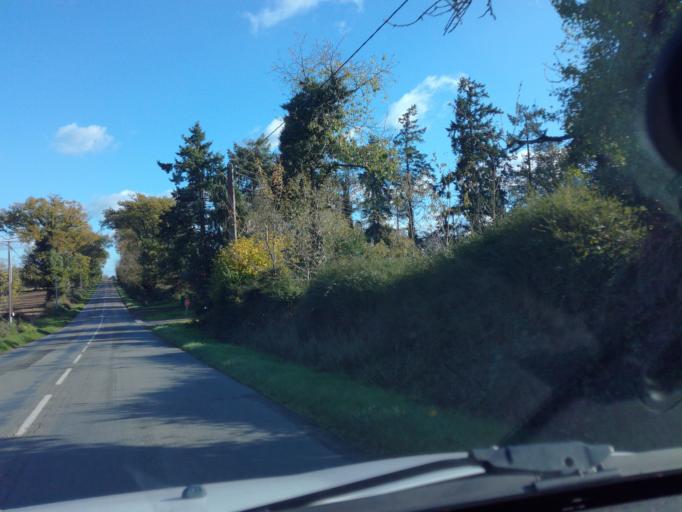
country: FR
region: Brittany
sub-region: Departement d'Ille-et-Vilaine
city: Chavagne
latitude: 48.0320
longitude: -1.8053
